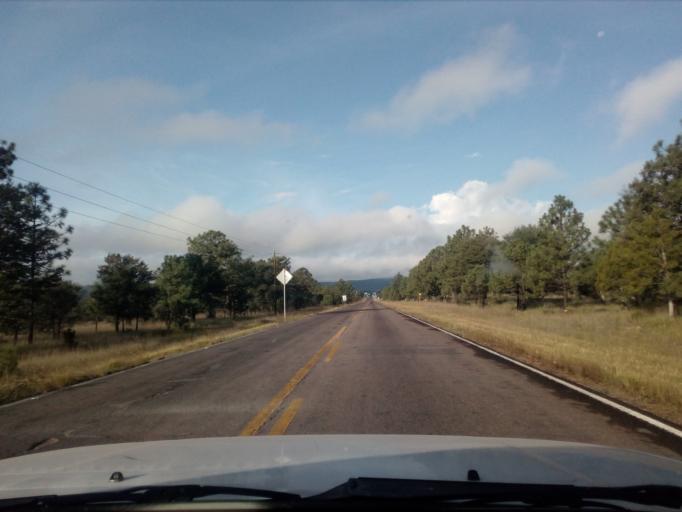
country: MX
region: Durango
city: Victoria de Durango
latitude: 23.9269
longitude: -104.9311
